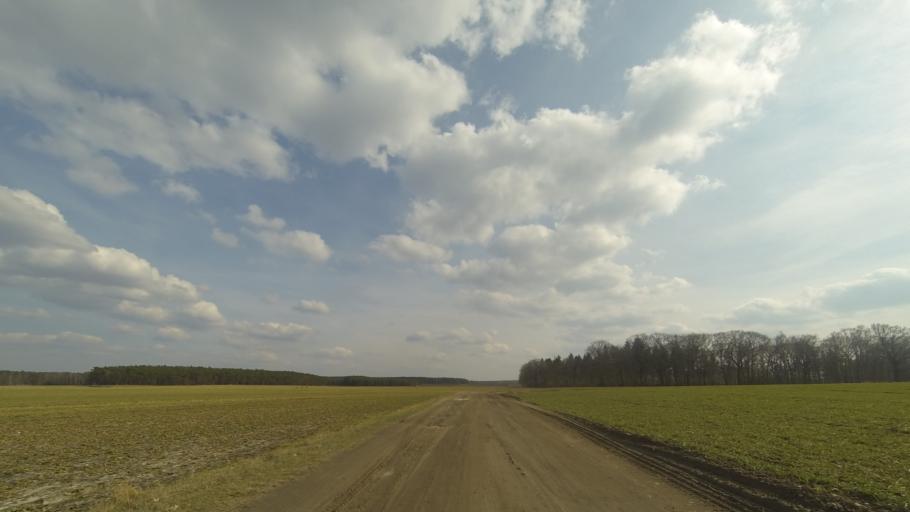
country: DE
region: Saxony
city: Radeburg
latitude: 51.2520
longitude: 13.7037
